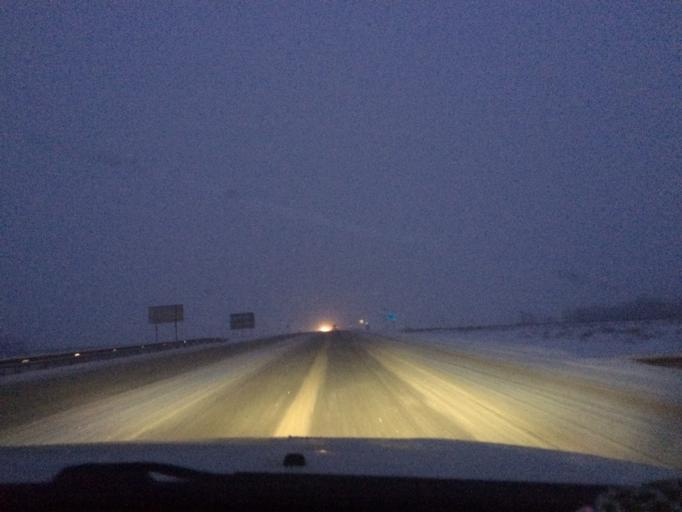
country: RU
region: Tula
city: Kosaya Gora
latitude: 54.1573
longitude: 37.5048
